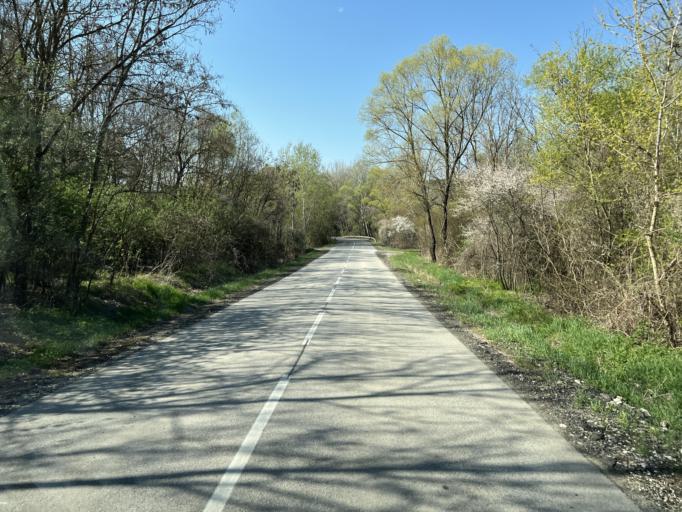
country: HU
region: Pest
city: Orbottyan
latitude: 47.7322
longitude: 19.2706
